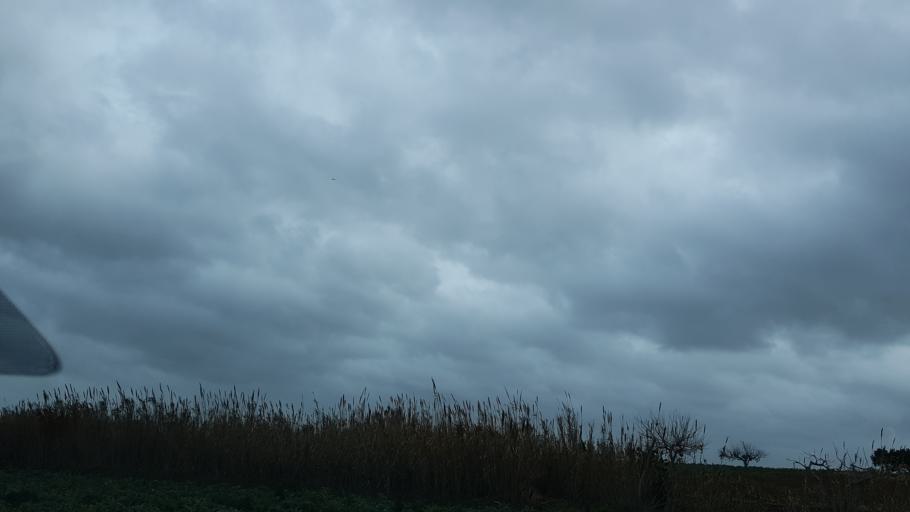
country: IT
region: Apulia
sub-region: Provincia di Brindisi
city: Brindisi
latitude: 40.6574
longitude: 17.8650
